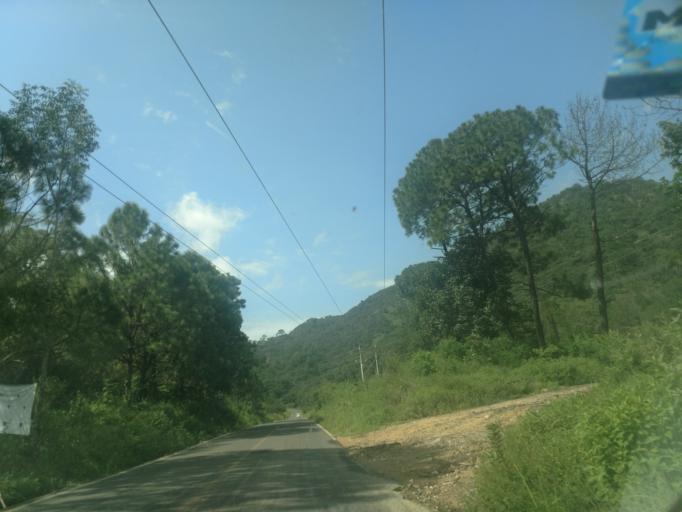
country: MX
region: Jalisco
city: Talpa de Allende
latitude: 20.4307
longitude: -104.7952
